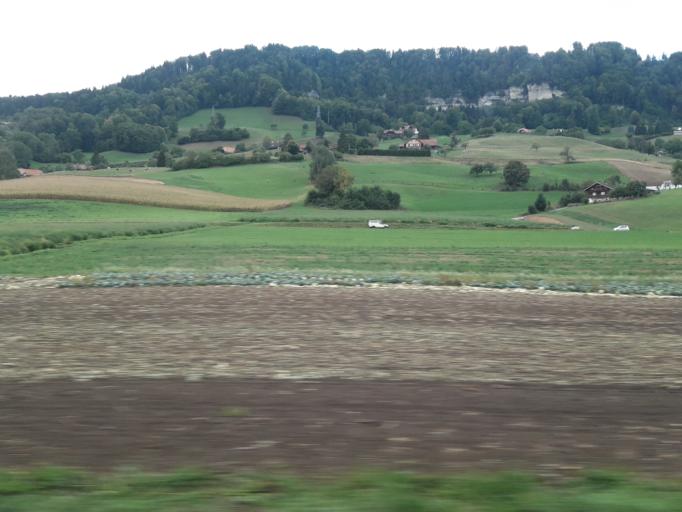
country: CH
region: Bern
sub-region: Bern-Mittelland District
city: Toffen
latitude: 46.8429
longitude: 7.4998
